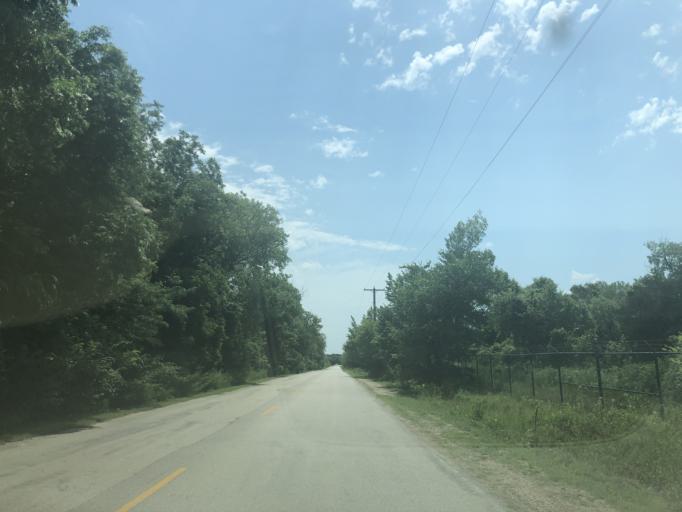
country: US
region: Texas
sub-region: Dallas County
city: Irving
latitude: 32.7866
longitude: -96.9405
